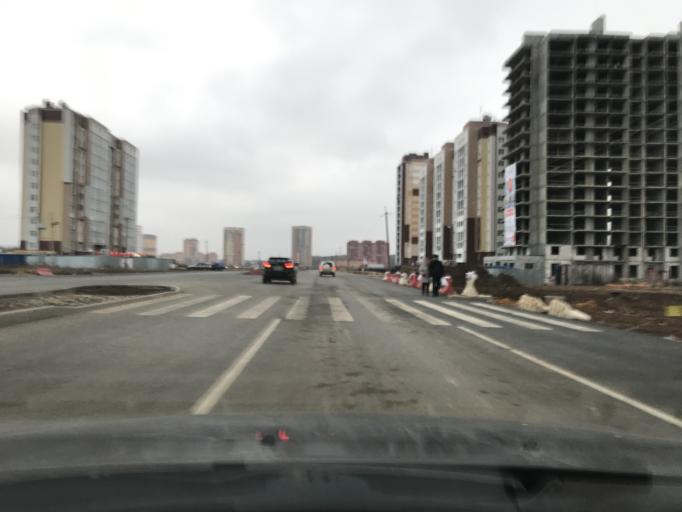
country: RU
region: Kaluga
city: Mstikhino
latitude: 54.4903
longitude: 36.1867
